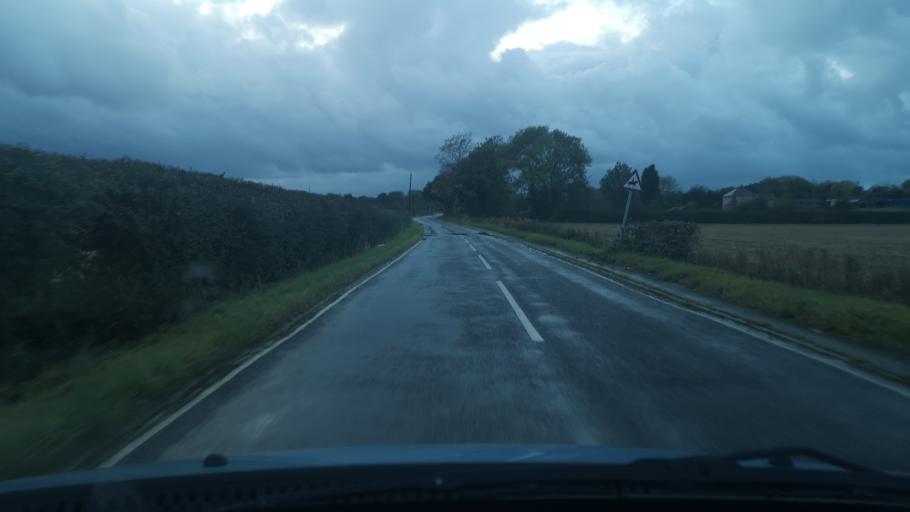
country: GB
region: England
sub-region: City and Borough of Wakefield
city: Badsworth
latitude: 53.6488
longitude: -1.3028
